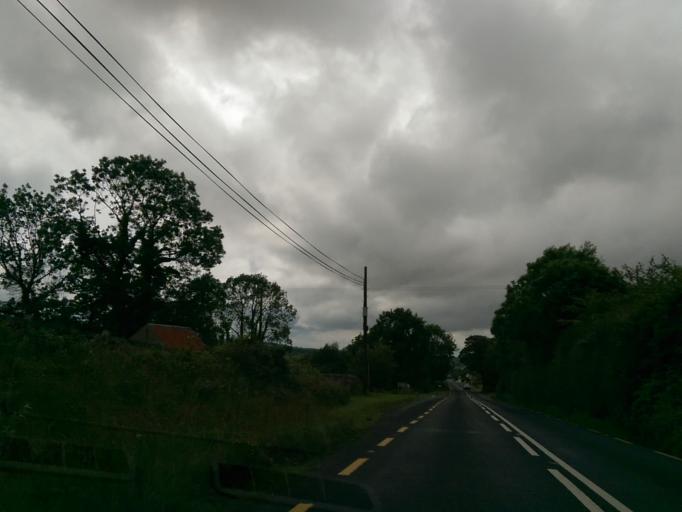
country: IE
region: Munster
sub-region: An Clar
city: Ennis
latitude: 52.7568
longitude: -9.1300
